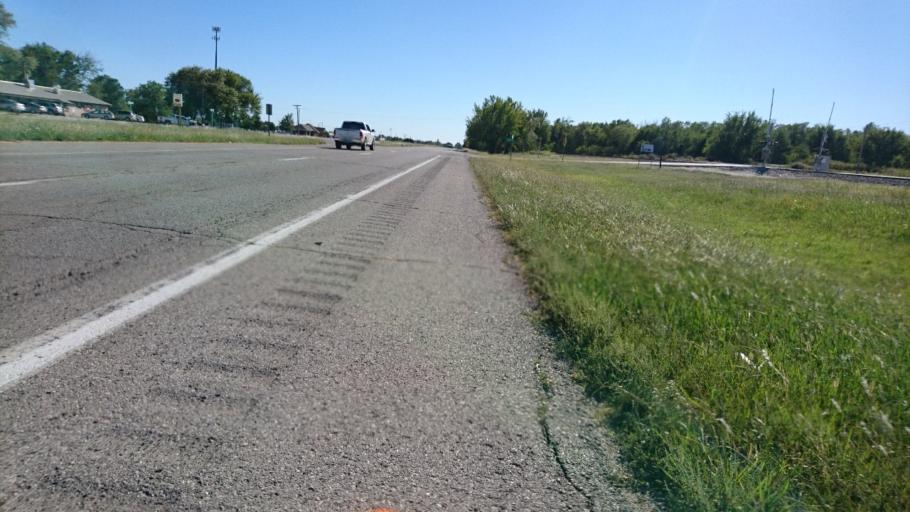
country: US
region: Oklahoma
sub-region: Rogers County
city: Justice
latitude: 36.3835
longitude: -95.5564
